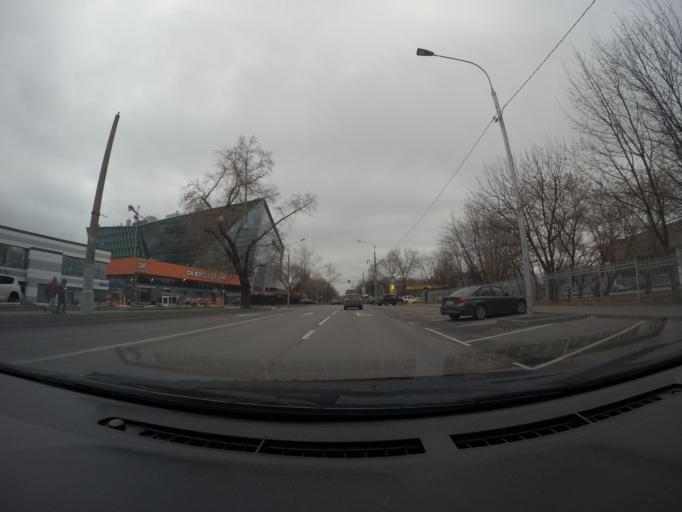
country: RU
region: Moscow
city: Ostankinskiy
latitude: 55.8190
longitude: 37.6170
